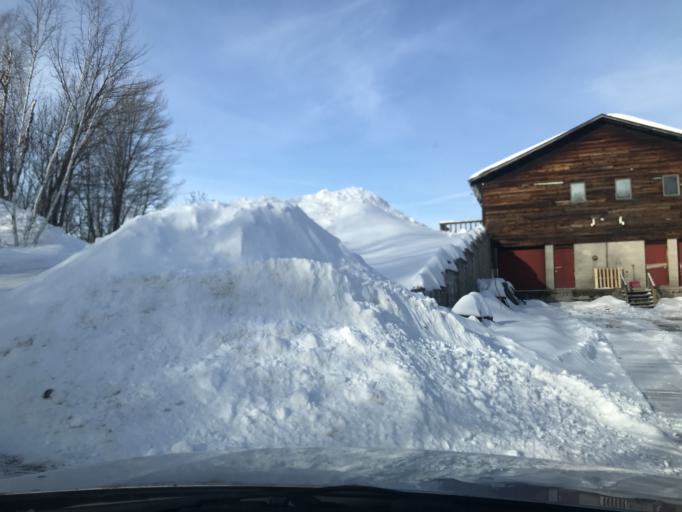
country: US
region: Wisconsin
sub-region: Menominee County
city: Legend Lake
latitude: 45.2994
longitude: -88.5300
